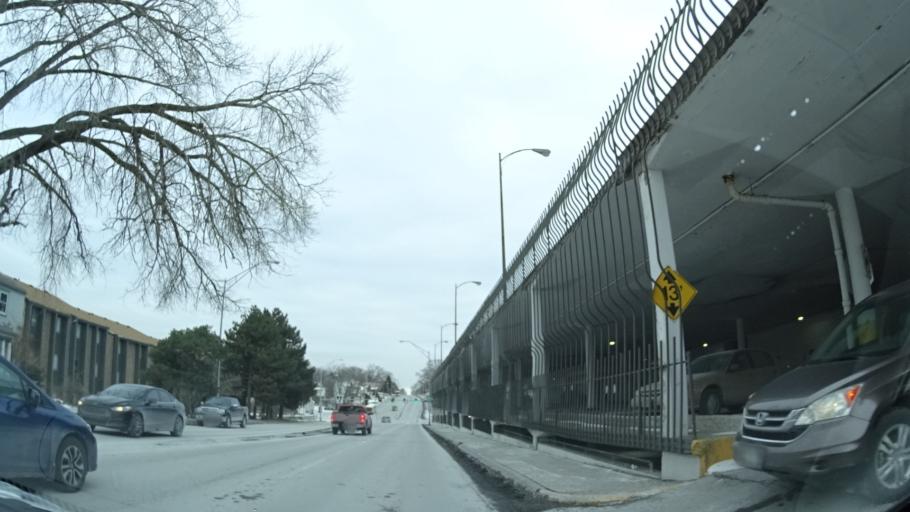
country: US
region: Nebraska
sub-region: Douglas County
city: Omaha
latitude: 41.2399
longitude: -95.9757
